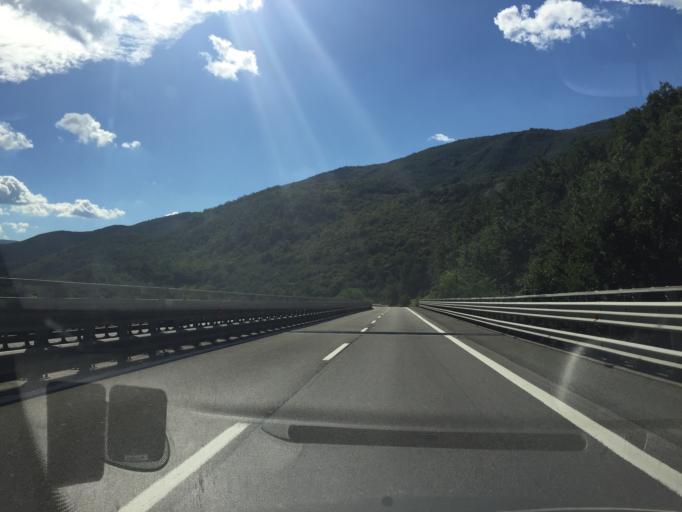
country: IT
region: Tuscany
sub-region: Provincia di Massa-Carrara
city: Pontremoli
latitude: 44.4409
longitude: 9.9044
